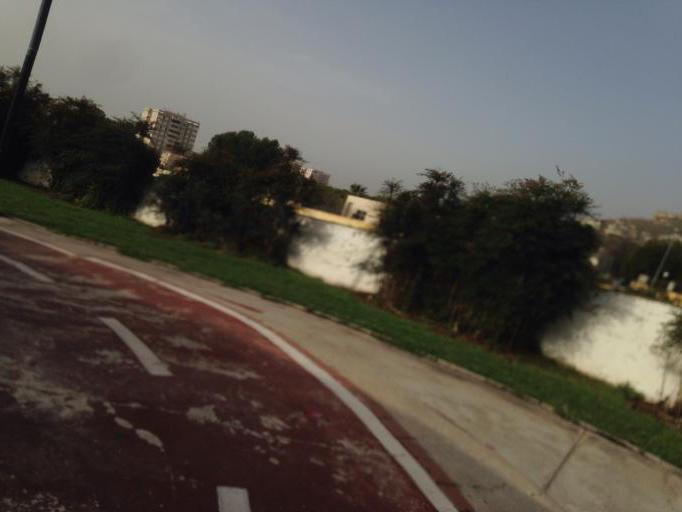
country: ES
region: Andalusia
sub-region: Provincia de Malaga
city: Malaga
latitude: 36.7386
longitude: -4.4247
